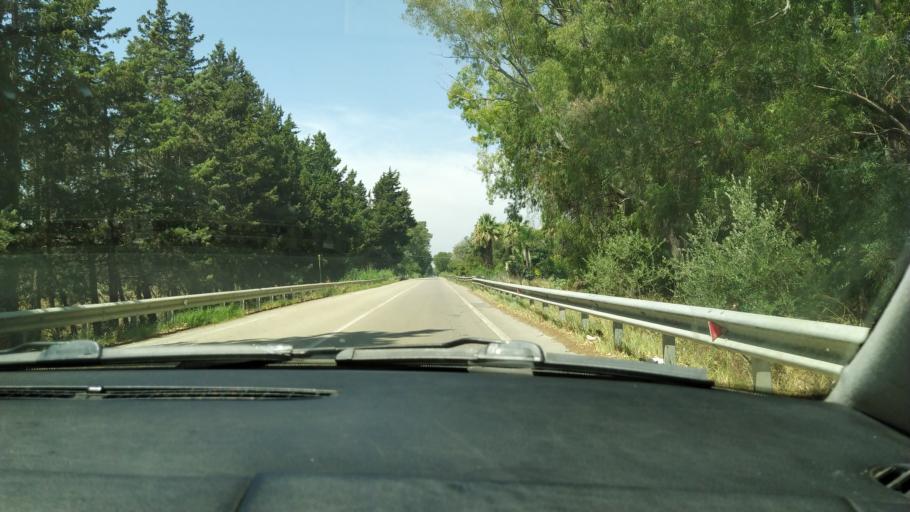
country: IT
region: Apulia
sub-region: Provincia di Taranto
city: Marina di Ginosa
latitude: 40.3722
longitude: 16.8061
